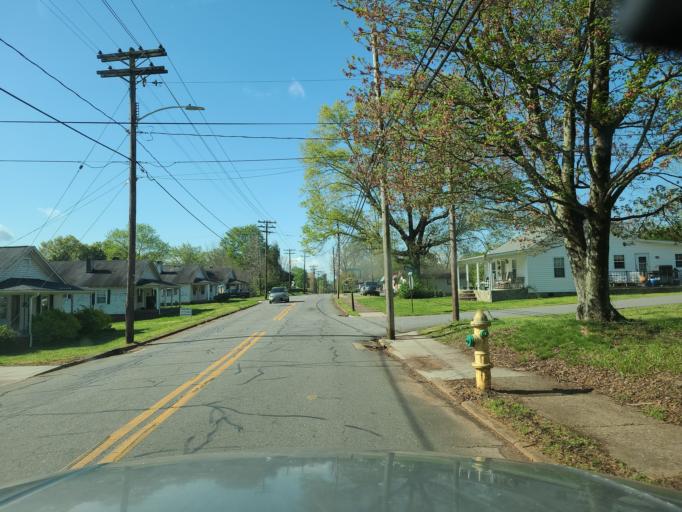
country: US
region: North Carolina
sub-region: Rutherford County
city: Spindale
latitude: 35.3687
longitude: -81.9268
